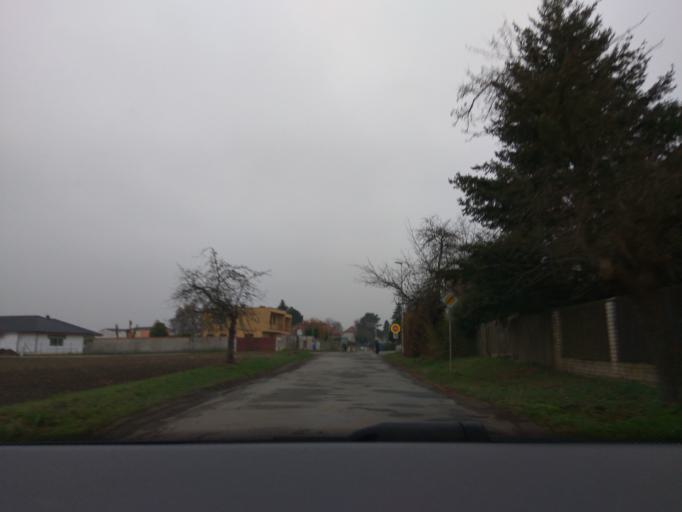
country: CZ
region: Praha
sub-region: Praha 19
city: Kbely
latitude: 50.1609
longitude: 14.5718
